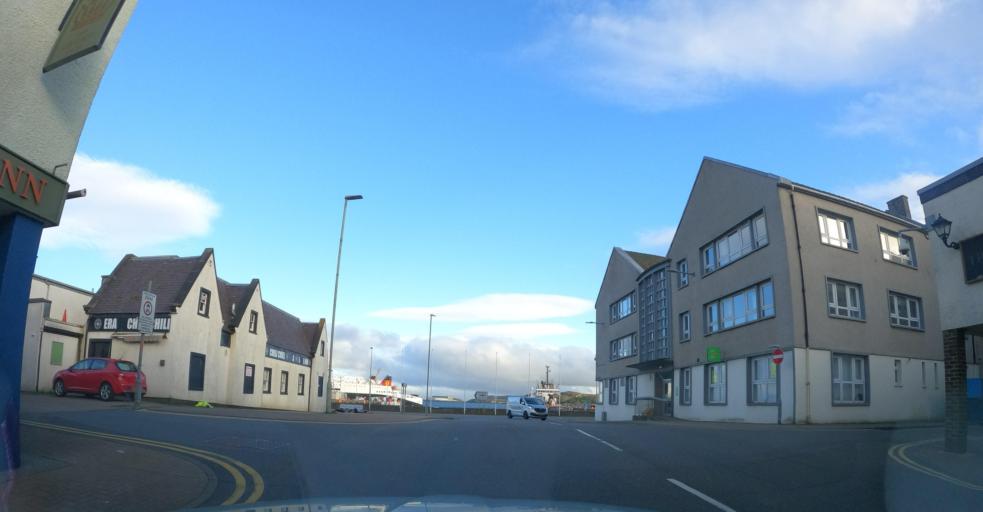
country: GB
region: Scotland
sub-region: Eilean Siar
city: Stornoway
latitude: 58.2082
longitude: -6.3906
